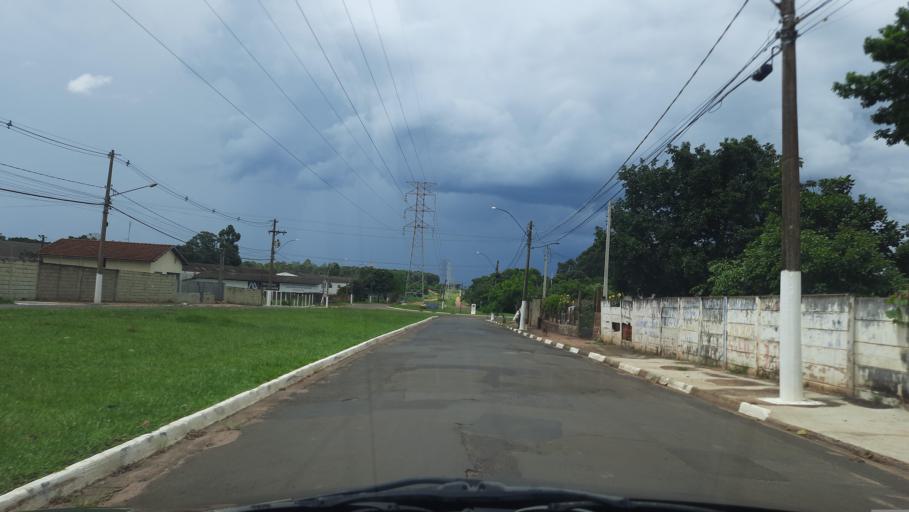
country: BR
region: Sao Paulo
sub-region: Casa Branca
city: Casa Branca
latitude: -21.7797
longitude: -47.0694
